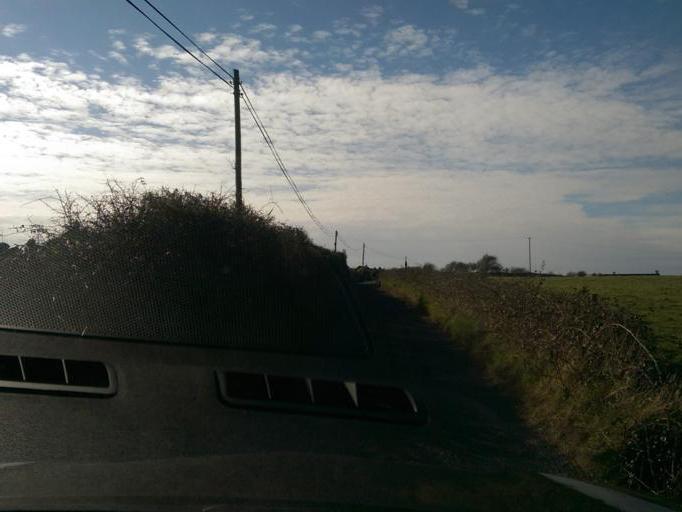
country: IE
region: Connaught
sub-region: County Galway
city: Oranmore
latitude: 53.2339
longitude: -8.9639
